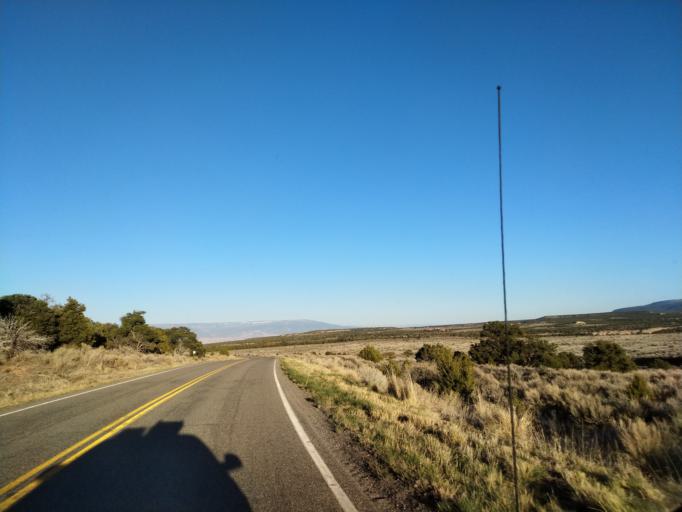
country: US
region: Colorado
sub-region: Mesa County
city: Redlands
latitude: 39.0050
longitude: -108.7011
